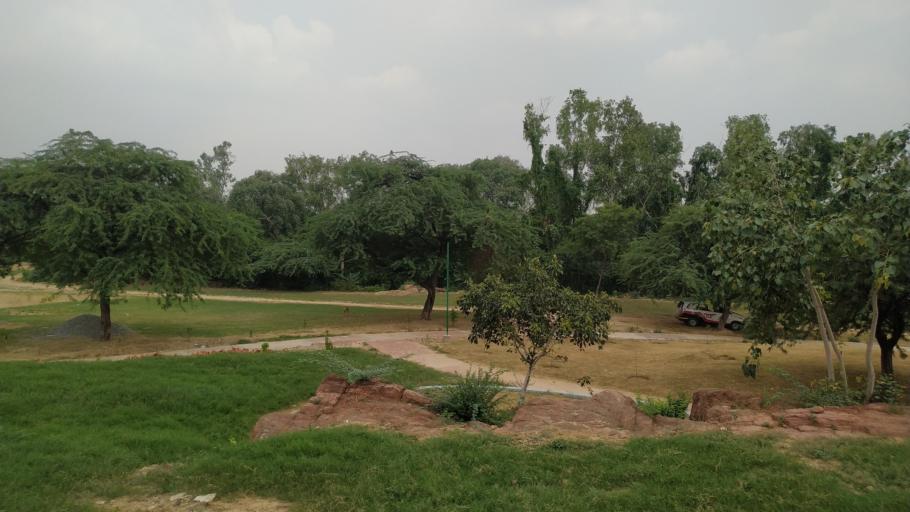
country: IN
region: NCT
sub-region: New Delhi
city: New Delhi
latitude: 28.5708
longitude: 77.2477
